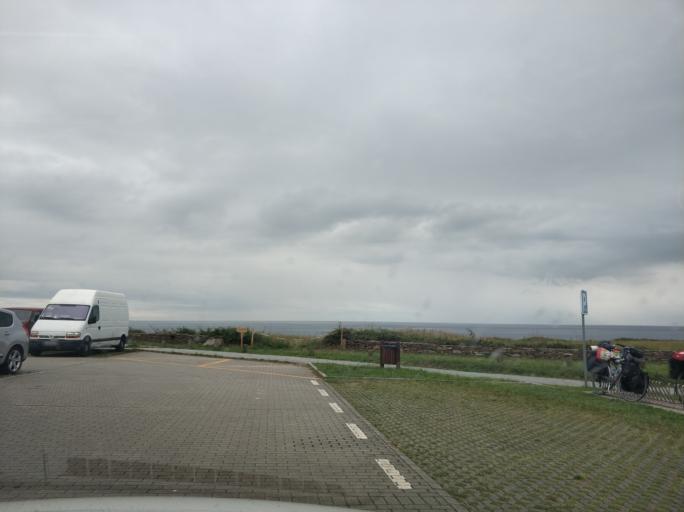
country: ES
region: Galicia
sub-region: Provincia de Lugo
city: Barreiros
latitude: 43.5527
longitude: -7.1565
